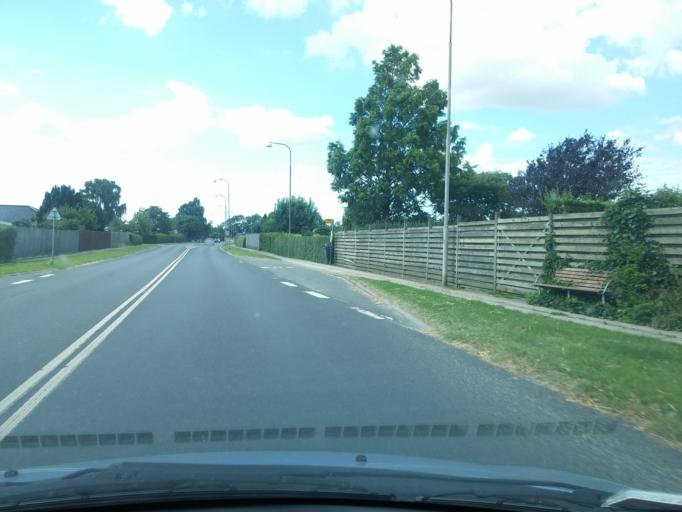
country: DK
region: South Denmark
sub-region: Odense Kommune
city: Bullerup
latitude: 55.4287
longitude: 10.4741
